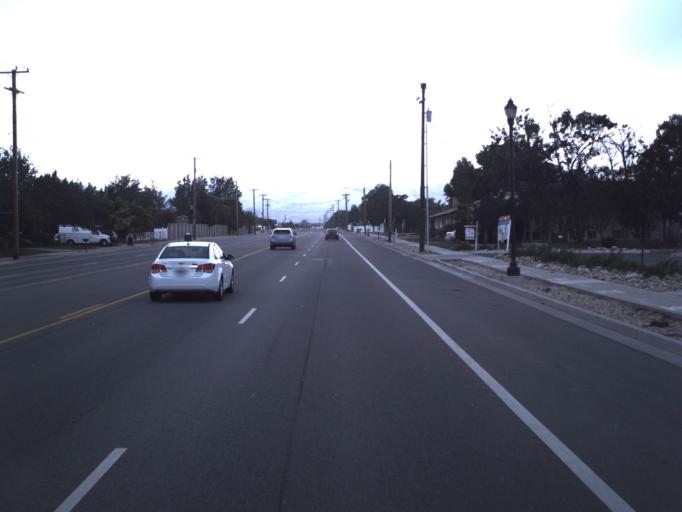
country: US
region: Utah
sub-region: Salt Lake County
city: Riverton
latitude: 40.5224
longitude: -111.9634
